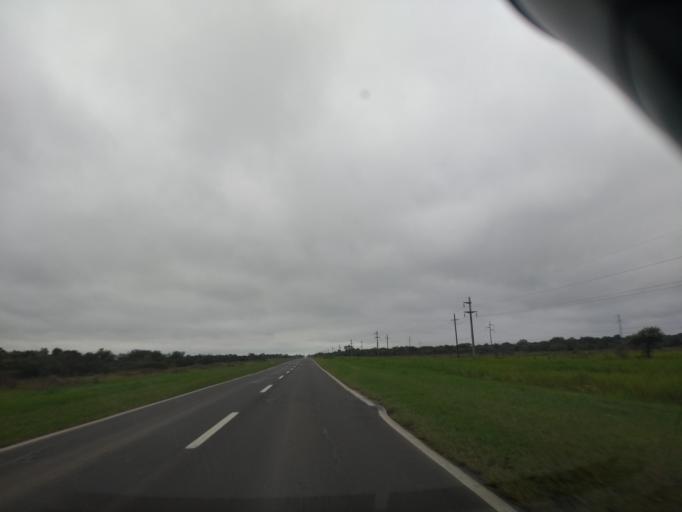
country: AR
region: Chaco
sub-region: Departamento de Quitilipi
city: Quitilipi
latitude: -26.8634
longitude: -60.2747
